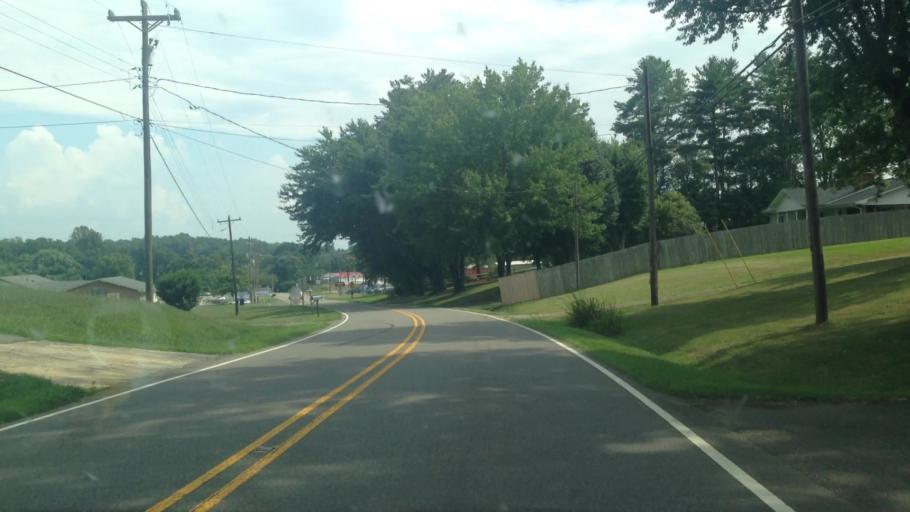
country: US
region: North Carolina
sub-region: Surry County
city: Flat Rock
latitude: 36.4738
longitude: -80.5744
